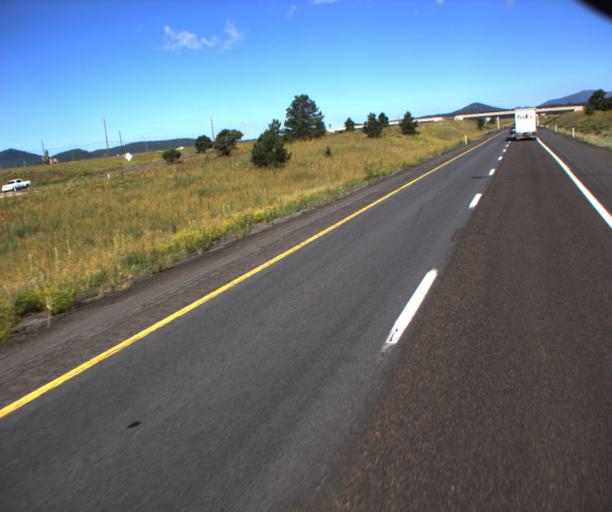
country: US
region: Arizona
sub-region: Coconino County
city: Parks
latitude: 35.2354
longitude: -111.8202
